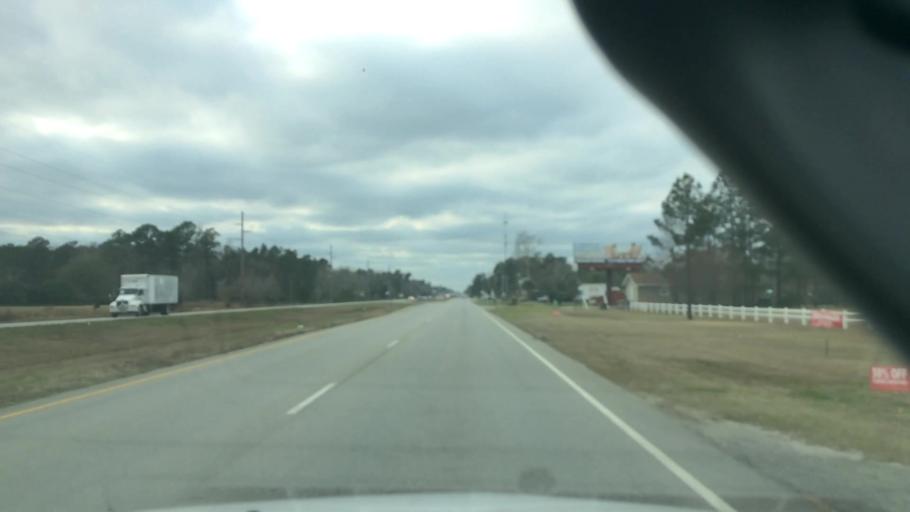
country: US
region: North Carolina
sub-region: Brunswick County
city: Sunset Beach
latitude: 33.9497
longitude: -78.4815
